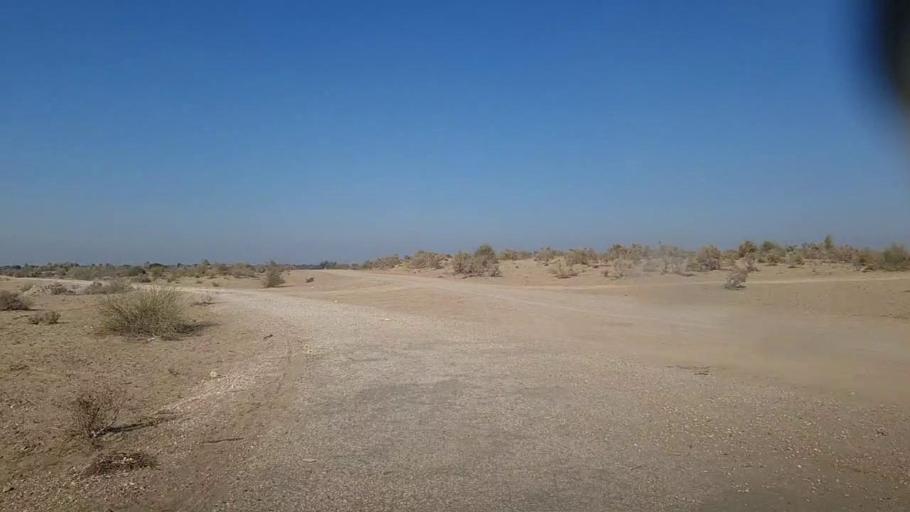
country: PK
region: Sindh
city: Khairpur
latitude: 27.9606
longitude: 69.8120
